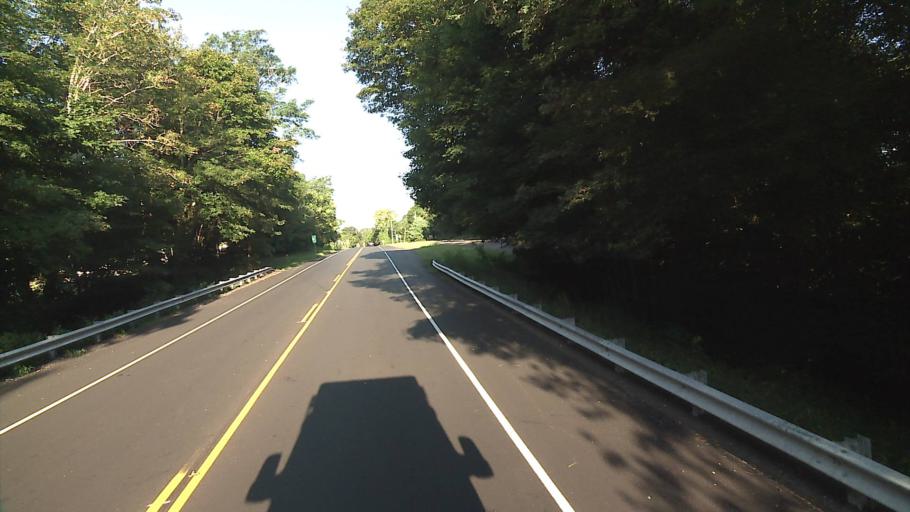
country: US
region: Connecticut
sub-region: New London County
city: Mystic
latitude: 41.3506
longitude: -71.9013
